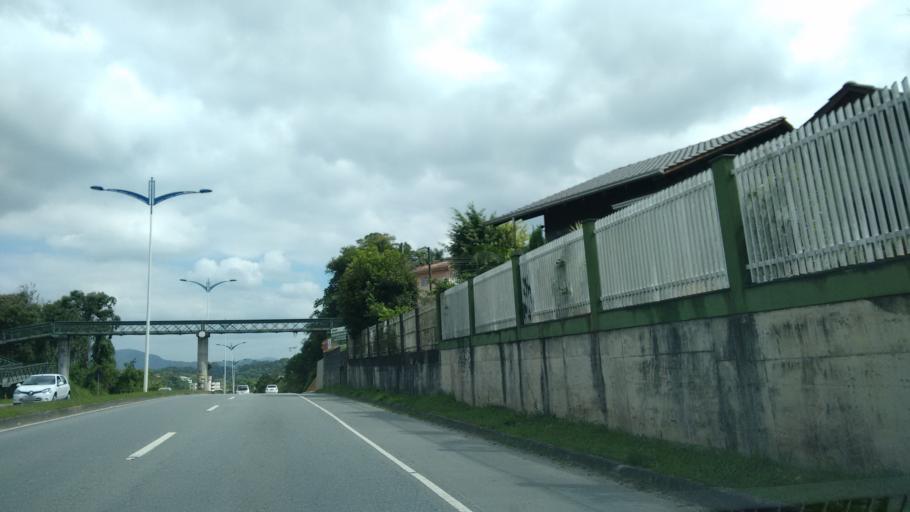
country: BR
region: Santa Catarina
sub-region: Blumenau
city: Blumenau
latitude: -26.8764
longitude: -49.0679
